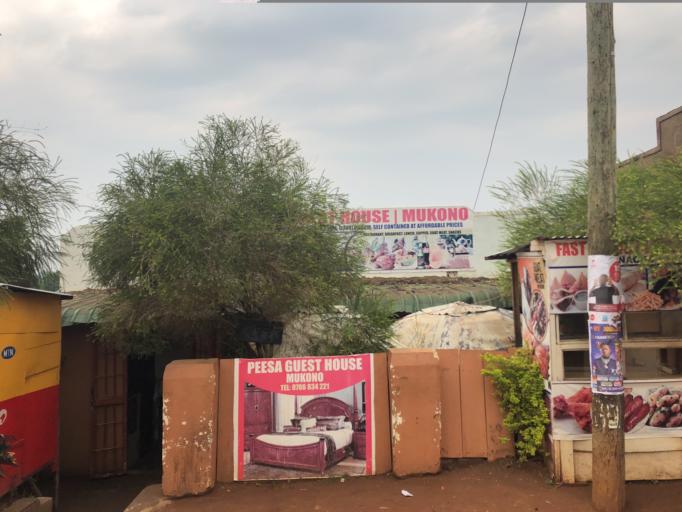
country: UG
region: Central Region
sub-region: Mukono District
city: Mukono
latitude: 0.3531
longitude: 32.7560
